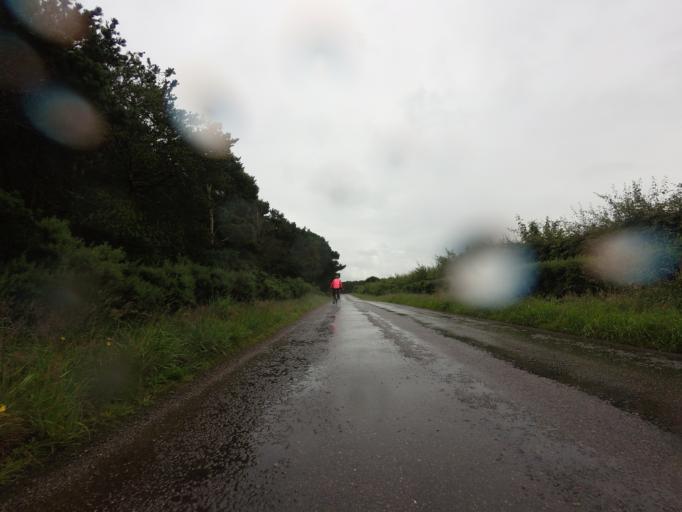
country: GB
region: Scotland
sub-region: Moray
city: Fochabers
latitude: 57.6654
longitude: -3.0752
